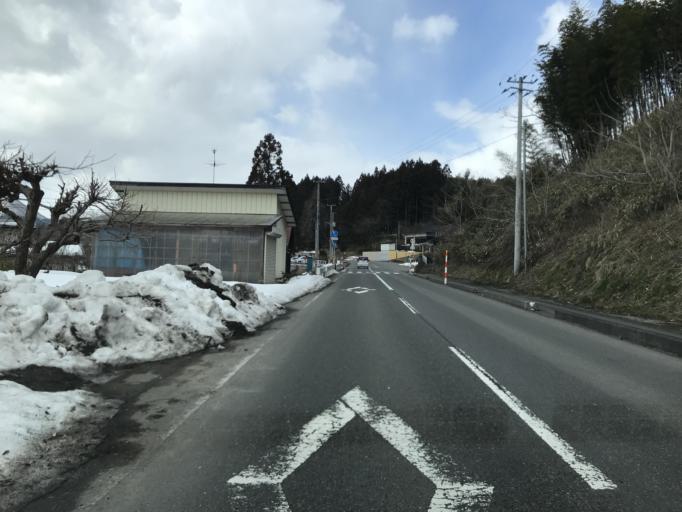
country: JP
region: Miyagi
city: Furukawa
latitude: 38.7365
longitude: 140.7701
